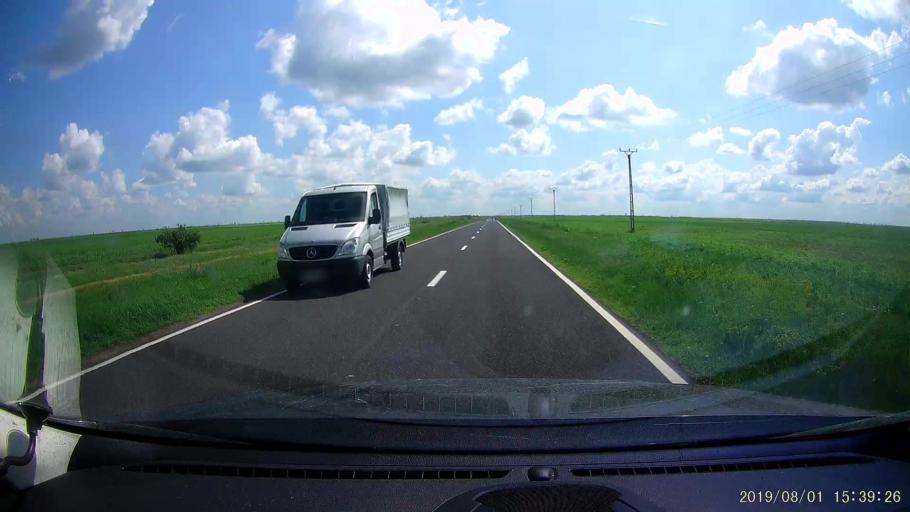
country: RO
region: Braila
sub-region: Comuna Victoria
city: Victoria
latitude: 44.8578
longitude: 27.5598
